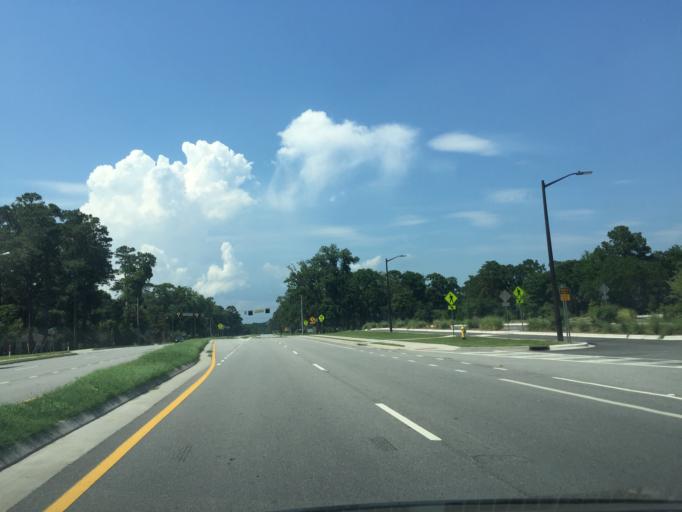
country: US
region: Georgia
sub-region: Chatham County
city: Montgomery
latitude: 31.9771
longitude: -81.1058
